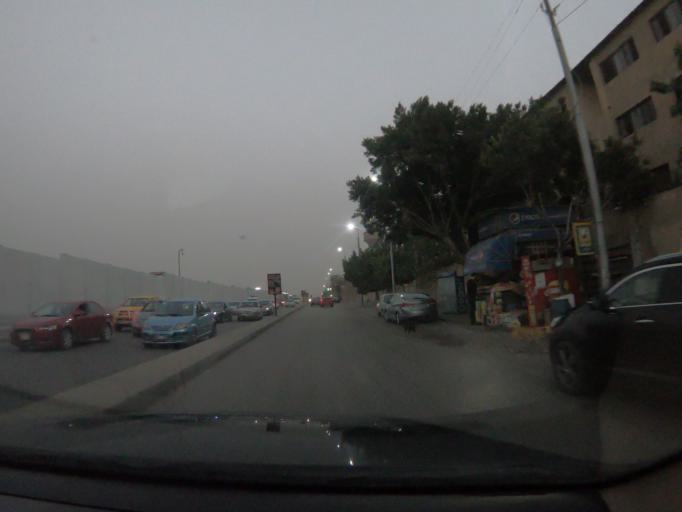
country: EG
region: Muhafazat al Qahirah
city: Cairo
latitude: 30.0897
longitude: 31.3489
